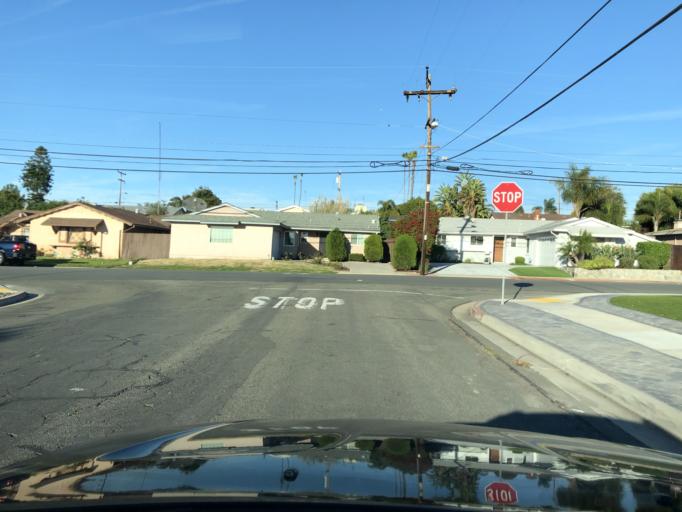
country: US
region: California
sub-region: San Diego County
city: La Jolla
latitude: 32.8211
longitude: -117.1879
